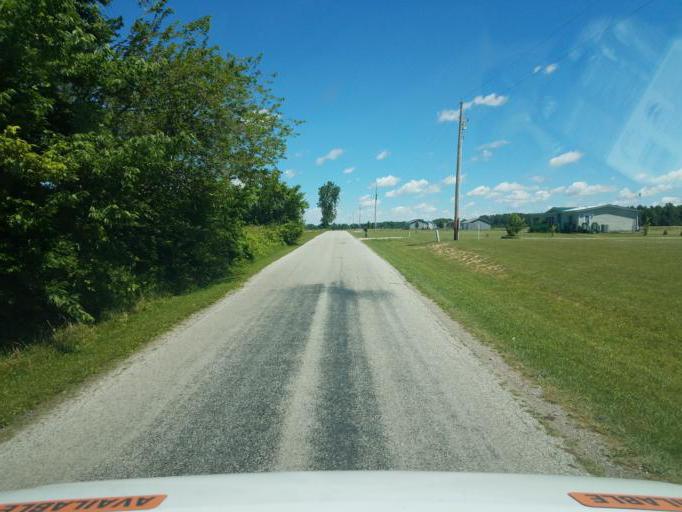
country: US
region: Ohio
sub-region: Morrow County
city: Mount Gilead
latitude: 40.6403
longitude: -82.9375
